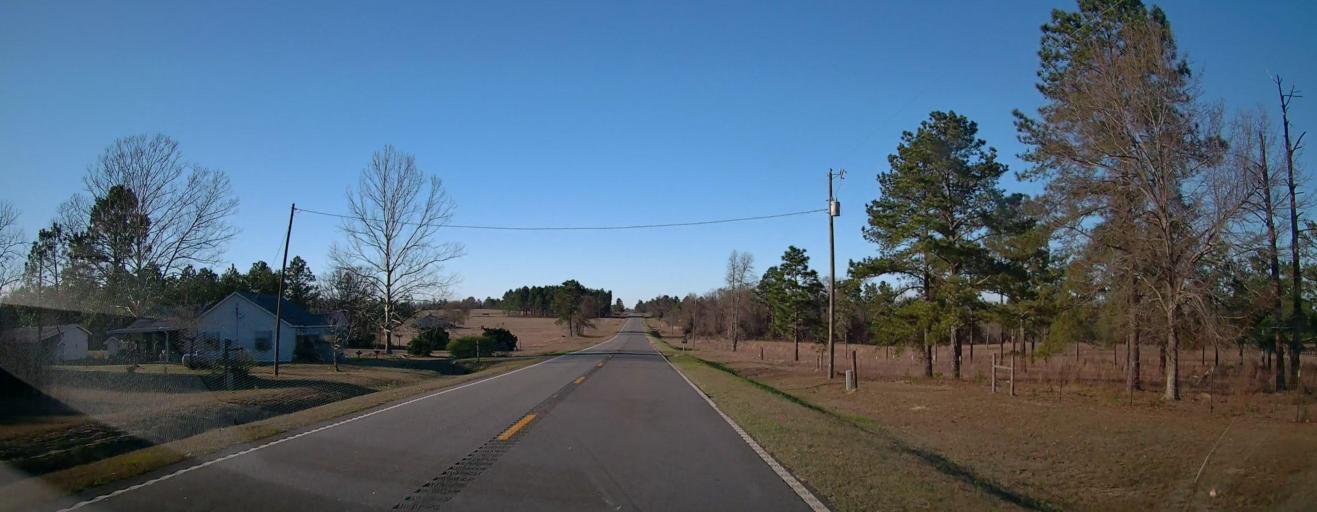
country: US
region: Georgia
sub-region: Taylor County
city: Butler
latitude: 32.5190
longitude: -84.4270
